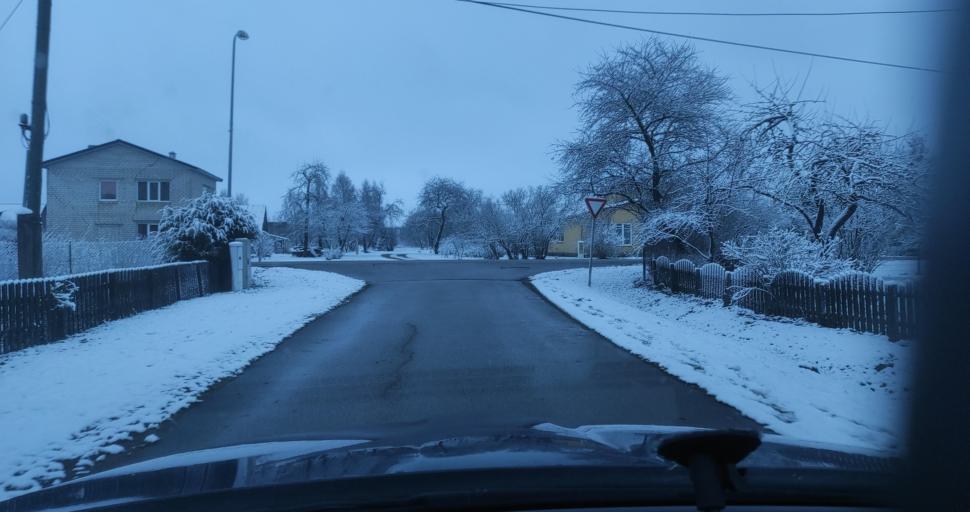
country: LV
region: Skrunda
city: Skrunda
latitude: 56.8700
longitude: 22.2341
